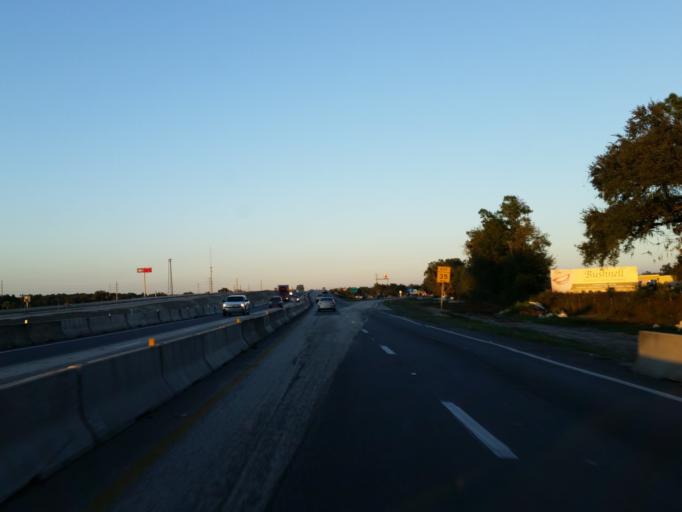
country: US
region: Florida
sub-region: Sumter County
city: Bushnell
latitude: 28.6649
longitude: -82.1452
